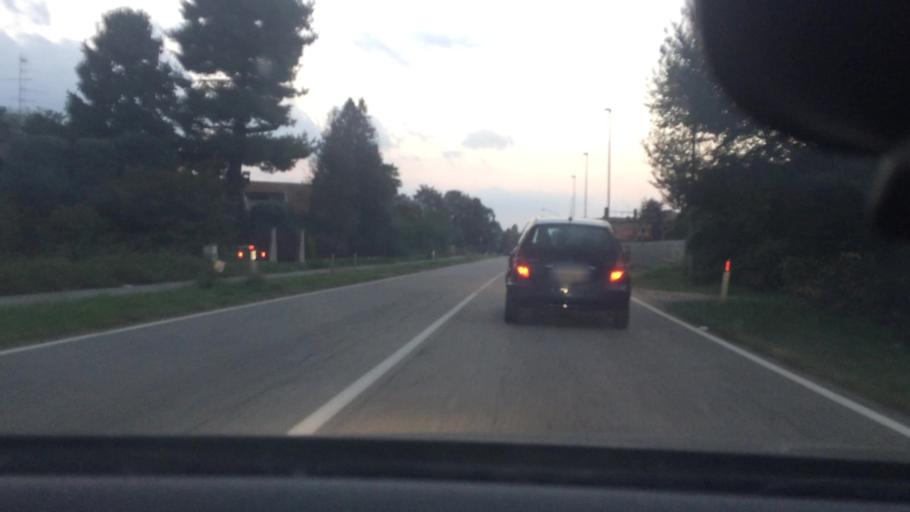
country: IT
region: Lombardy
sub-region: Citta metropolitana di Milano
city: Buscate
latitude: 45.5446
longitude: 8.8025
